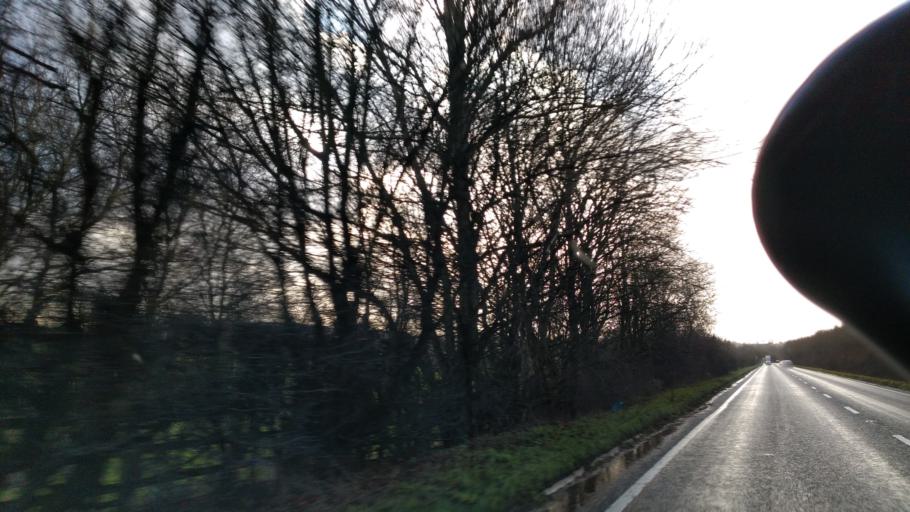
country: GB
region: England
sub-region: Somerset
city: Frome
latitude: 51.2214
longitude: -2.3034
